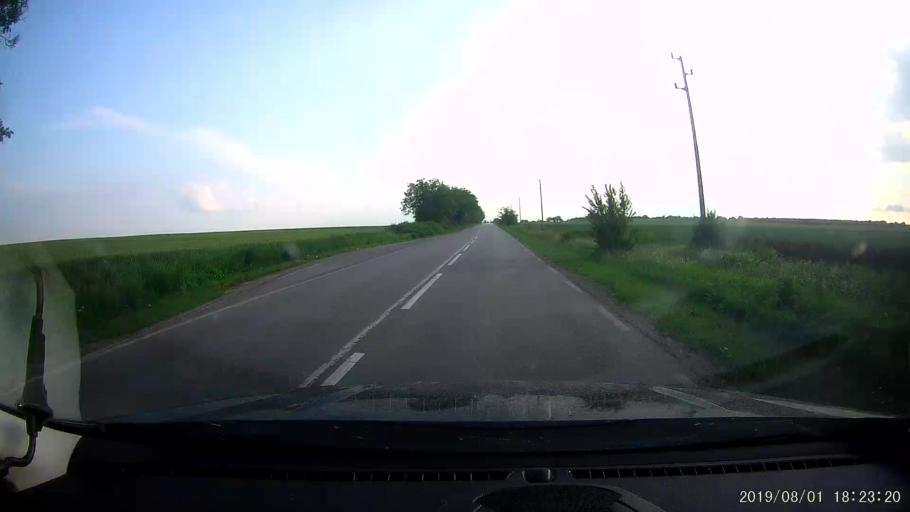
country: BG
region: Shumen
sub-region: Obshtina Kaolinovo
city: Kaolinovo
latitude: 43.6308
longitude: 27.0273
